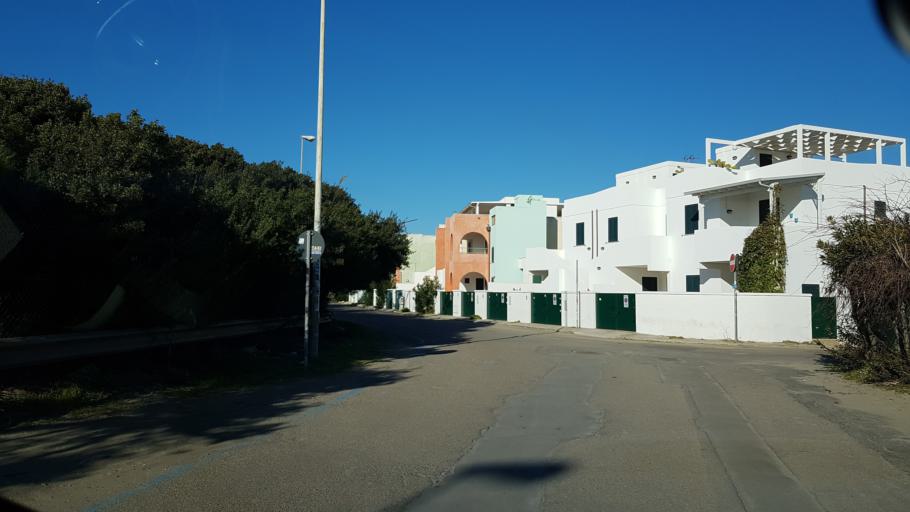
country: IT
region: Apulia
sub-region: Provincia di Lecce
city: Gallipoli
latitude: 40.0343
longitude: 18.0170
